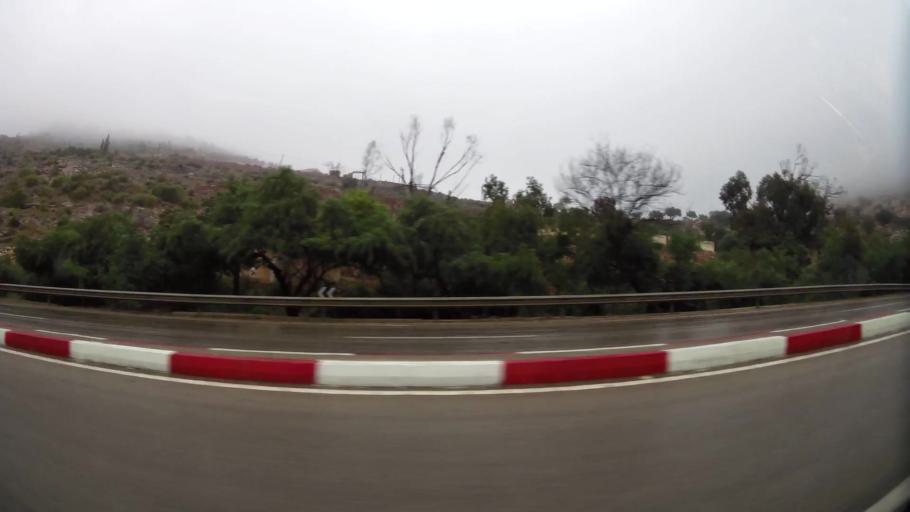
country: MA
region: Taza-Al Hoceima-Taounate
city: Al Hoceima
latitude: 35.2193
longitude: -3.9222
